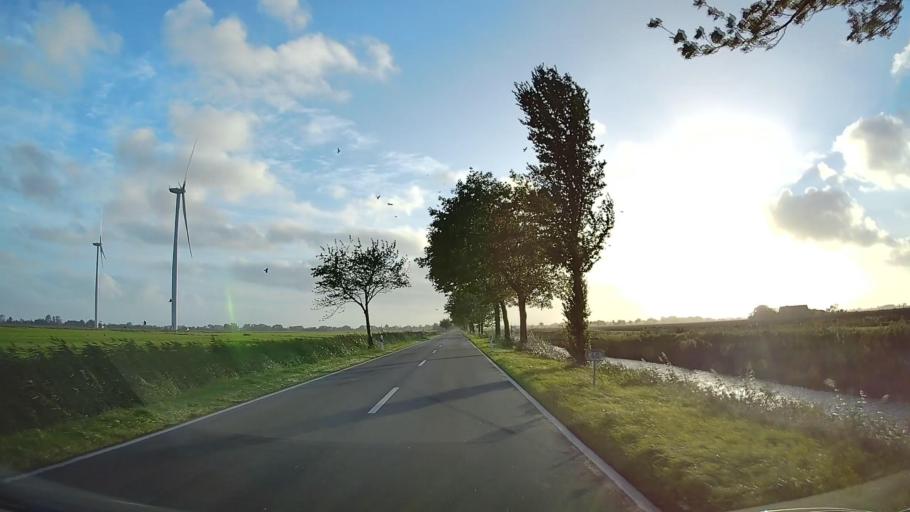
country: DE
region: Schleswig-Holstein
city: Sommerland
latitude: 53.7993
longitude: 9.5222
